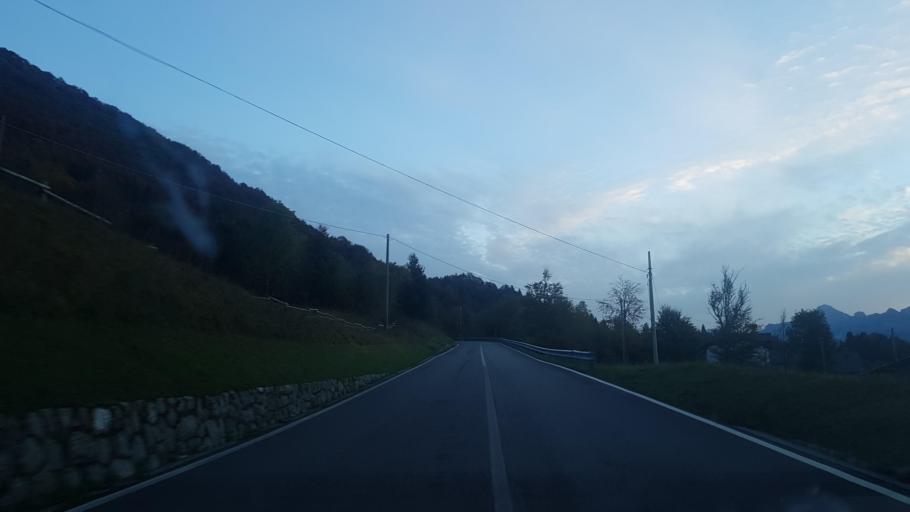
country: IT
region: Friuli Venezia Giulia
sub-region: Provincia di Udine
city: Chiaulis
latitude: 46.3643
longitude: 12.9551
